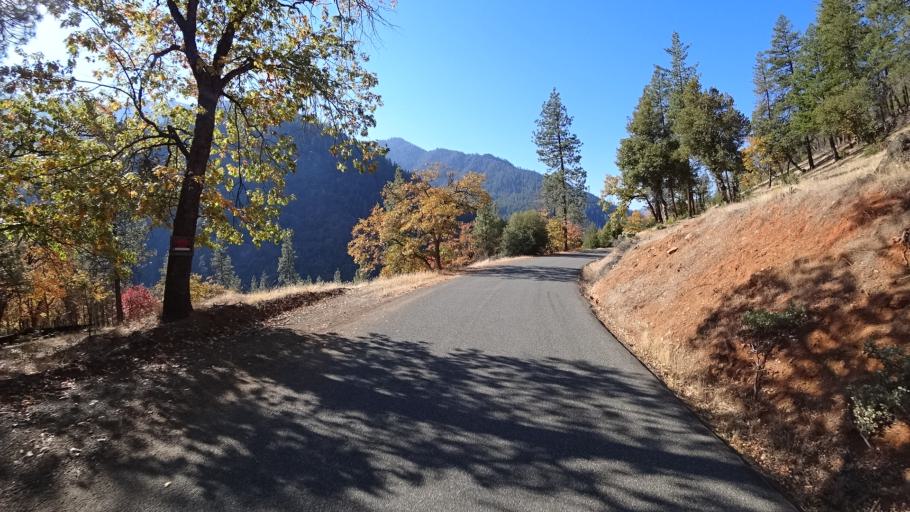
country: US
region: California
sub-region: Siskiyou County
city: Happy Camp
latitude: 41.7011
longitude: -123.0442
